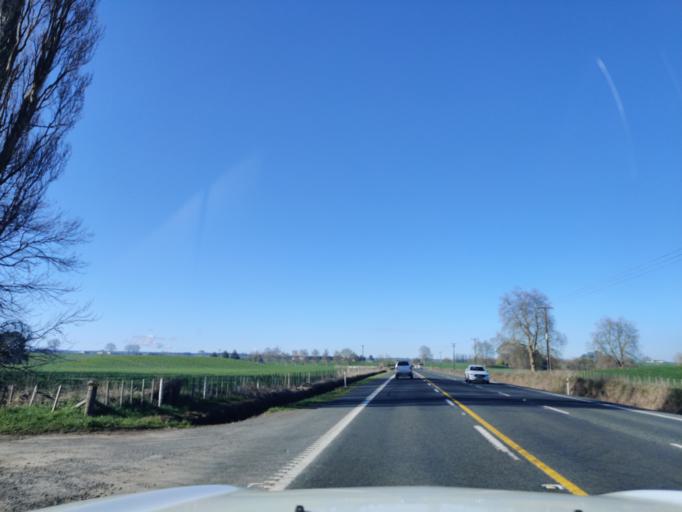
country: NZ
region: Waikato
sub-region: Matamata-Piako District
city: Matamata
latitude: -38.0187
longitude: 175.7812
